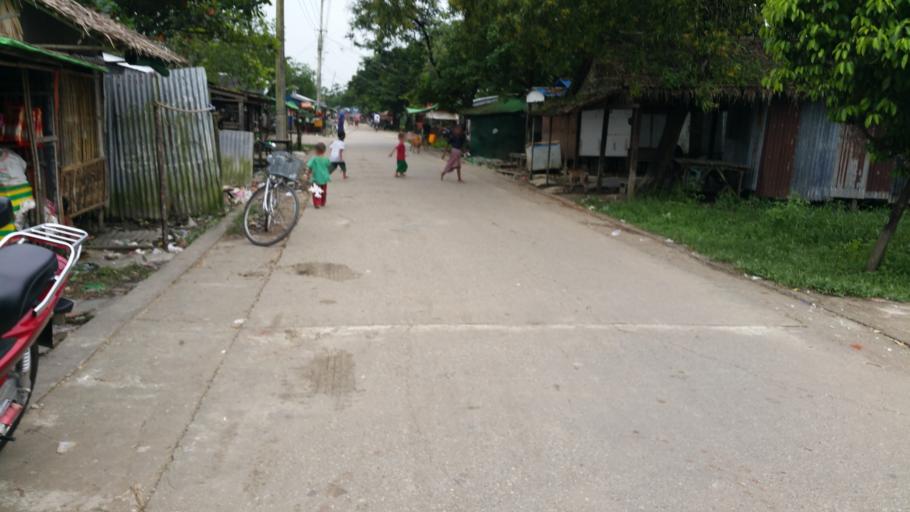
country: MM
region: Yangon
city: Yangon
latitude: 16.7639
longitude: 96.1385
